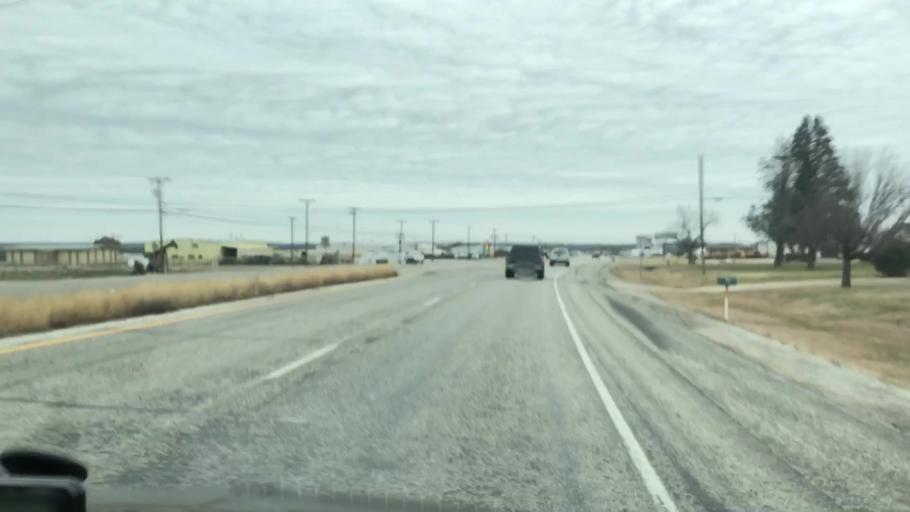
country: US
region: Texas
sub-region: Jack County
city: Jacksboro
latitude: 33.1965
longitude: -98.1460
